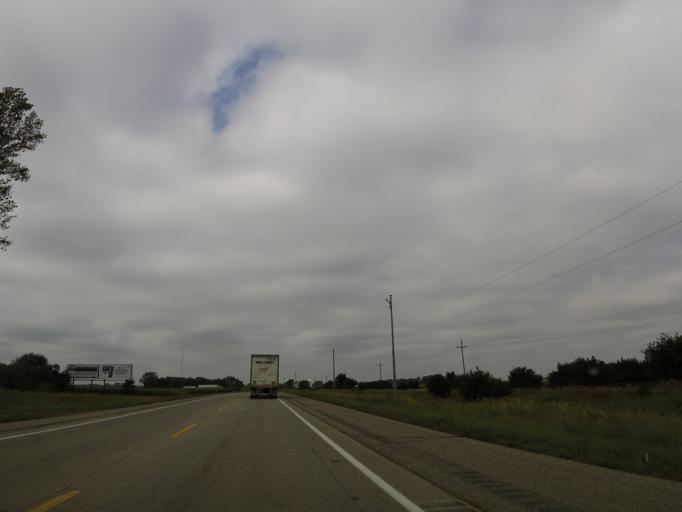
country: US
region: Minnesota
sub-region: Renville County
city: Olivia
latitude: 44.7748
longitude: -94.9607
